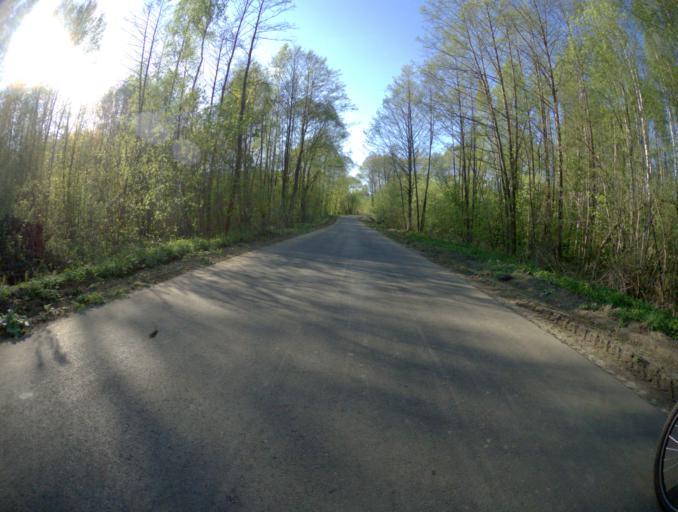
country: RU
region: Vladimir
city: Raduzhnyy
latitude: 56.0081
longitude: 40.3598
